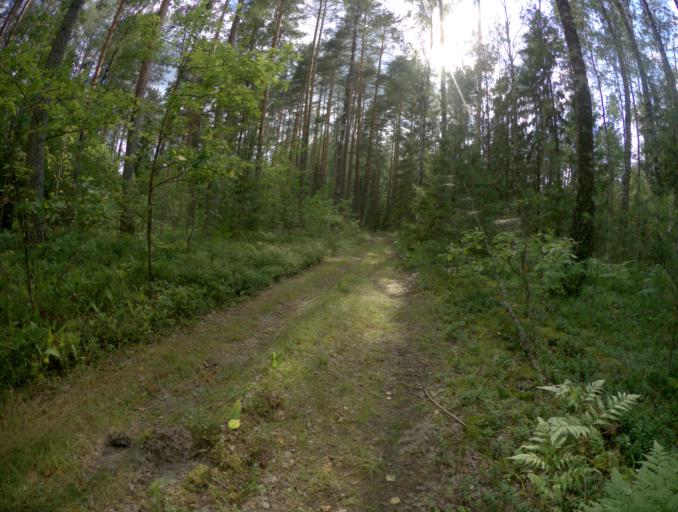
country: RU
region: Vladimir
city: Orgtrud
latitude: 56.1317
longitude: 40.6024
